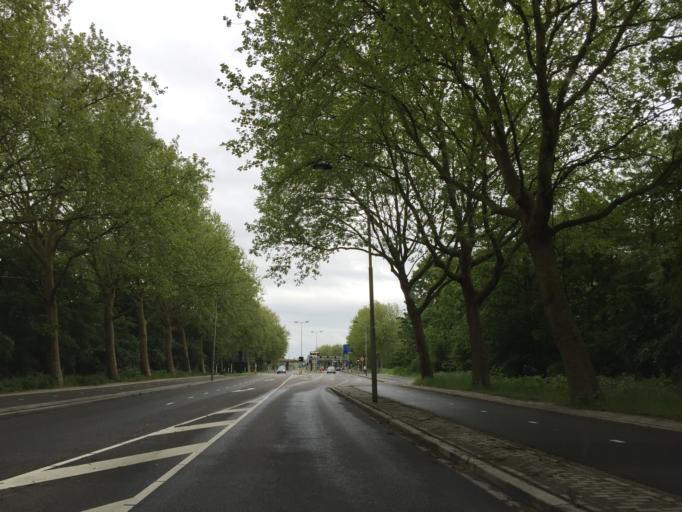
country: NL
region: South Holland
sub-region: Gemeente Delft
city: Delft
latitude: 51.9975
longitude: 4.3802
